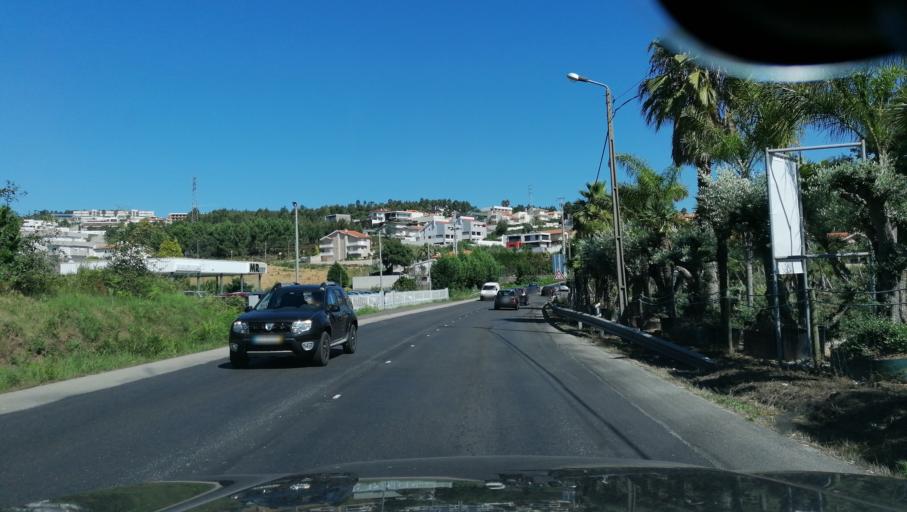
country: PT
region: Aveiro
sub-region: Santa Maria da Feira
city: Arrifana
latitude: 40.9302
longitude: -8.5140
